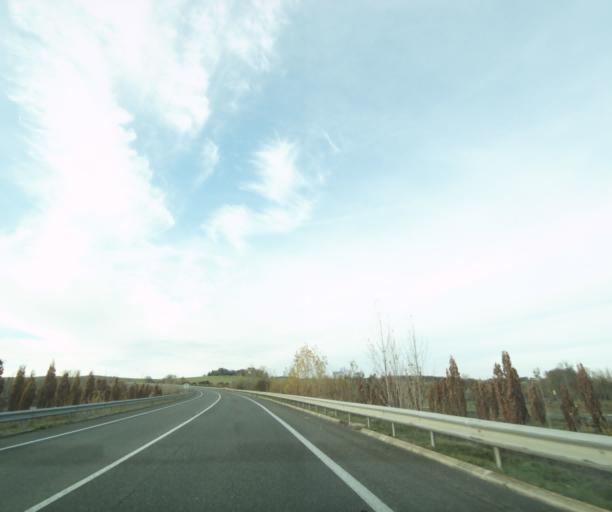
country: FR
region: Midi-Pyrenees
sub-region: Departement du Gers
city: Auch
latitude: 43.6652
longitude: 0.6203
